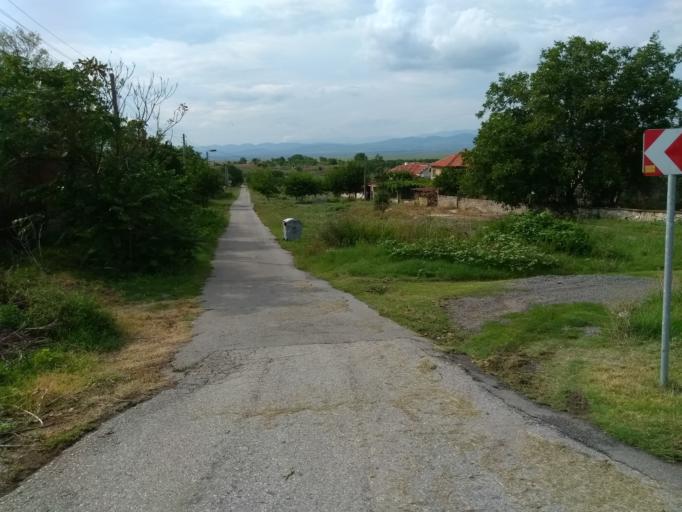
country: BG
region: Sliven
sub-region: Obshtina Sliven
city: Kermen
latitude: 42.4592
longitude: 26.1407
